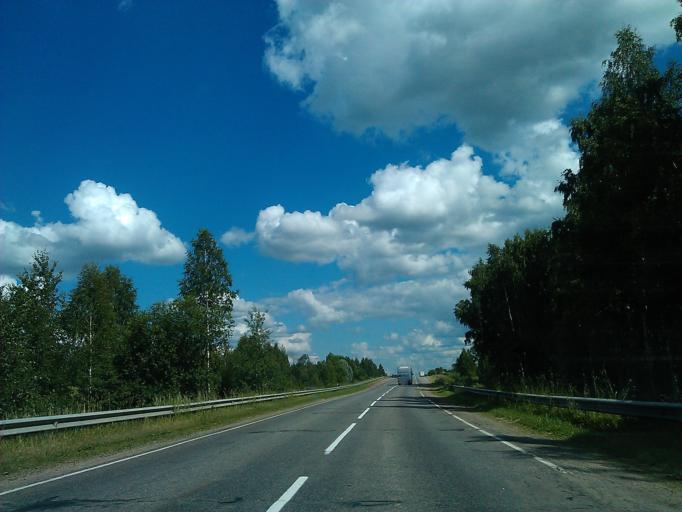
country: LV
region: Rezekne
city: Rezekne
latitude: 56.5487
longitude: 27.3349
